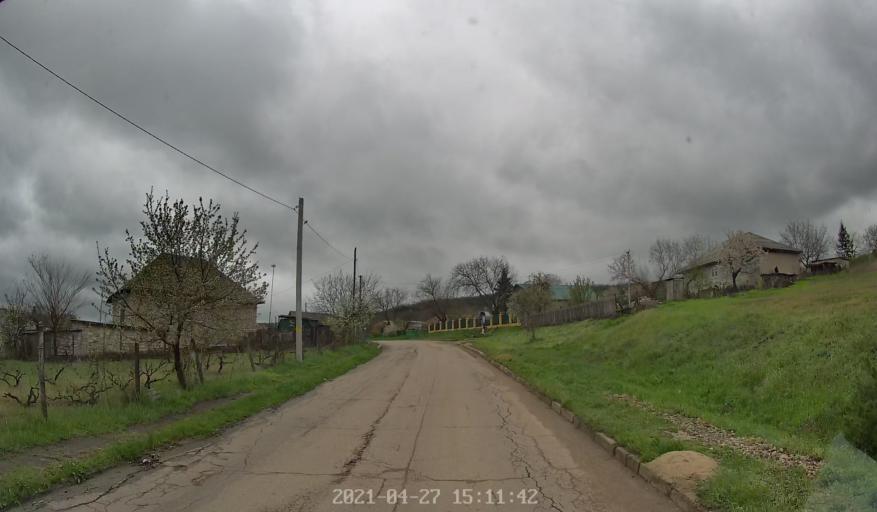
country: MD
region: Chisinau
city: Vadul lui Voda
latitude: 47.0302
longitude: 29.0253
